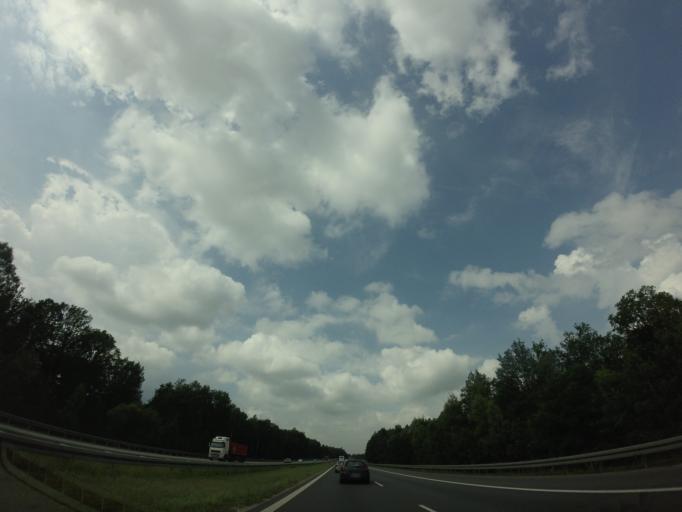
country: PL
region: Silesian Voivodeship
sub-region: Myslowice
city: Myslowice
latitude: 50.2191
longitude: 19.1096
